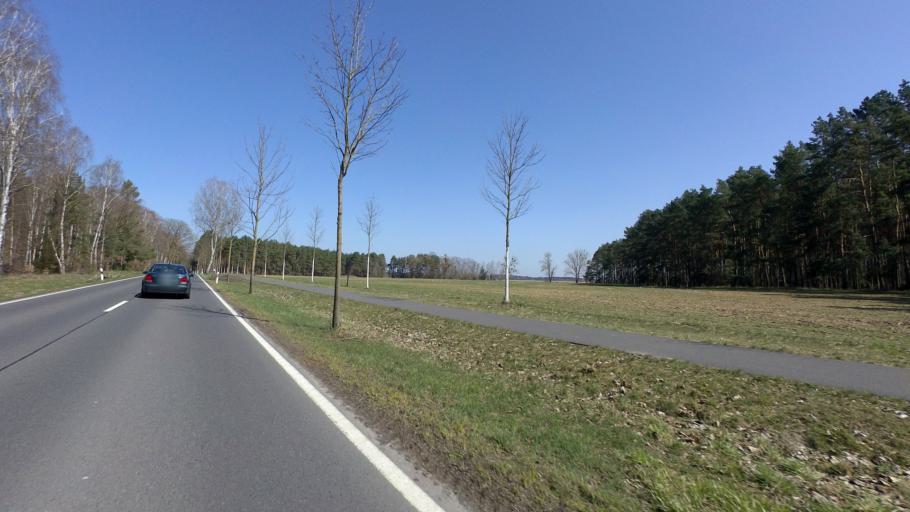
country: DE
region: Brandenburg
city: Lindow
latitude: 52.9430
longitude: 12.9715
